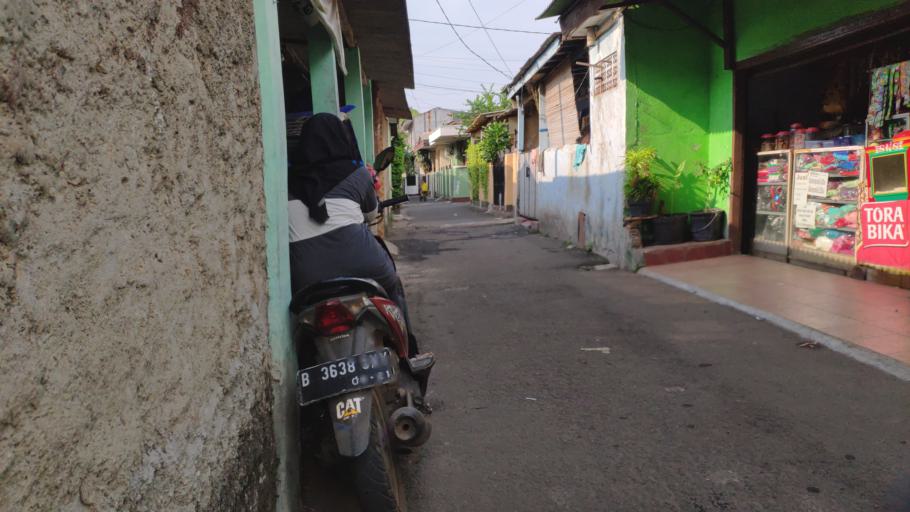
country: ID
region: West Java
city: Pamulang
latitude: -6.3100
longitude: 106.7986
